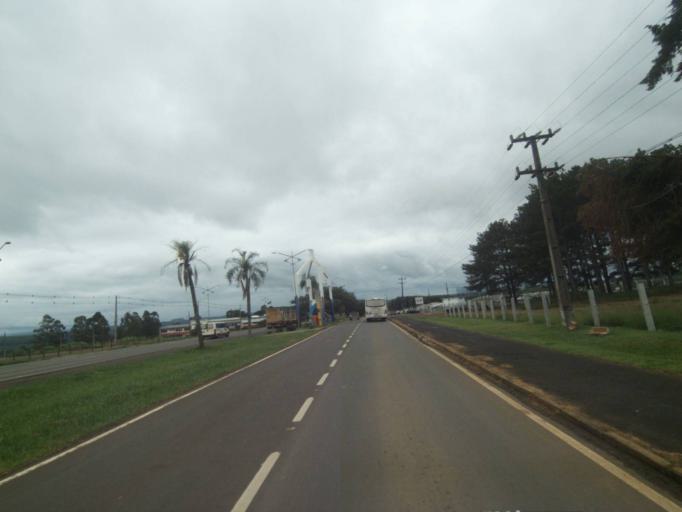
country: BR
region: Parana
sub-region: Telemaco Borba
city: Telemaco Borba
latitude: -24.3405
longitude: -50.6567
